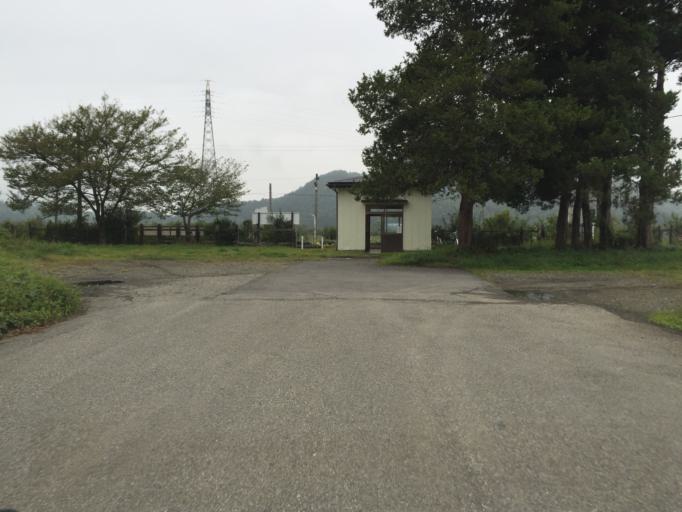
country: JP
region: Fukushima
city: Kitakata
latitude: 37.4425
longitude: 139.9142
